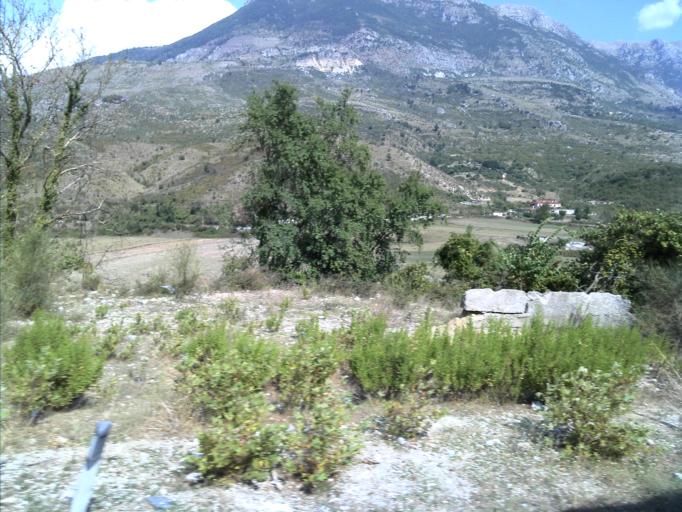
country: AL
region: Gjirokaster
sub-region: Rrethi i Tepelenes
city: Tepelene
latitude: 40.2592
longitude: 20.0538
